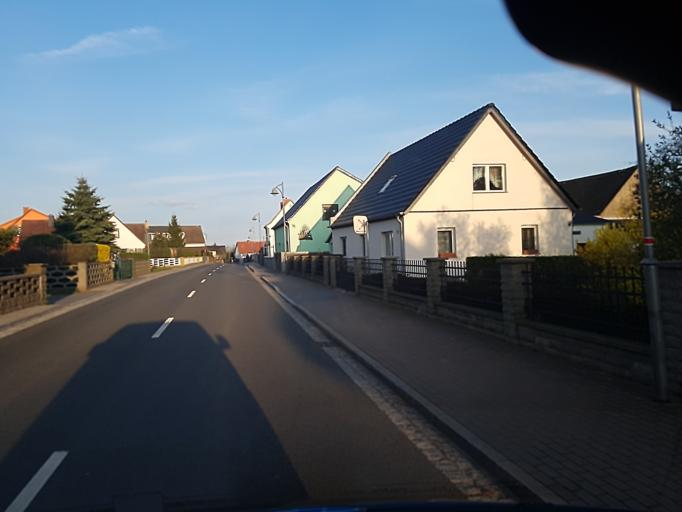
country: DE
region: Saxony
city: Elsnig
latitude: 51.5623
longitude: 12.8860
